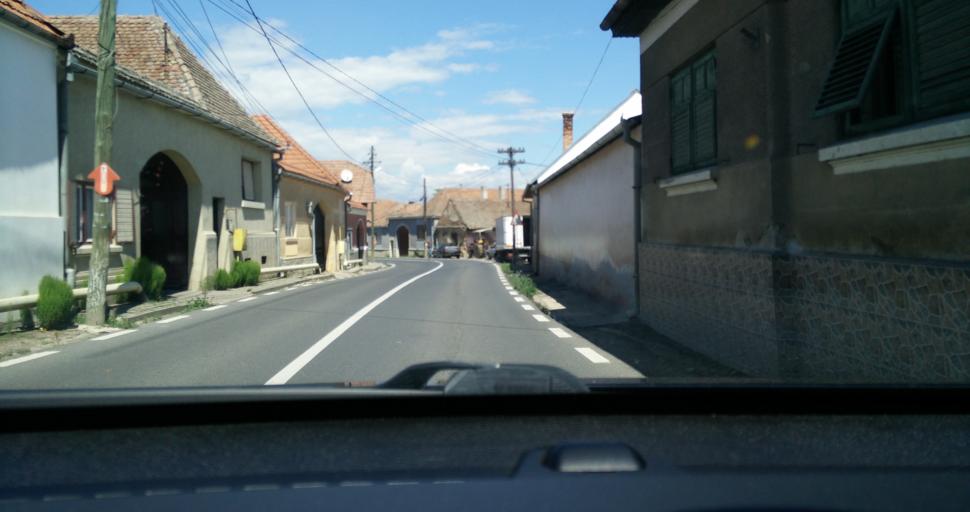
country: RO
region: Alba
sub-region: Comuna Sasciori
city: Sebesel
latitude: 45.8853
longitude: 23.5658
